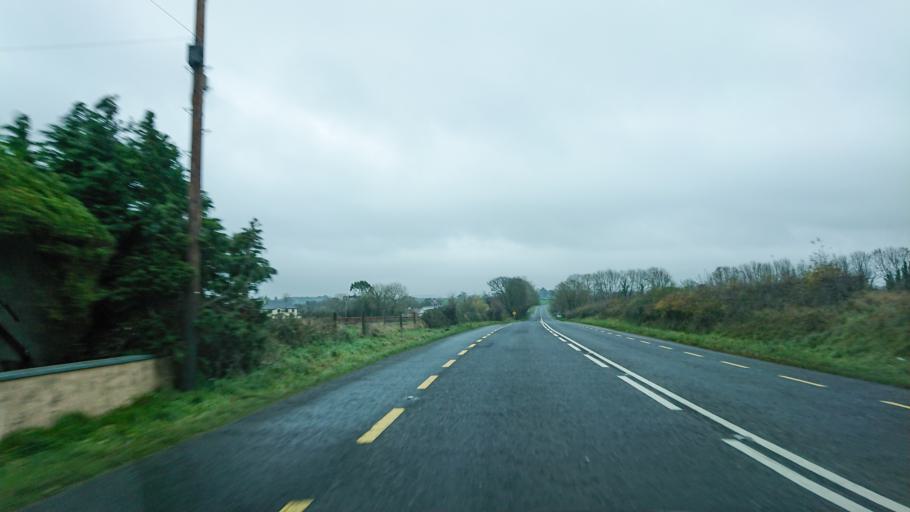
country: IE
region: Leinster
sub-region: Kilkenny
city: Mooncoin
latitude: 52.2868
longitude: -7.2195
